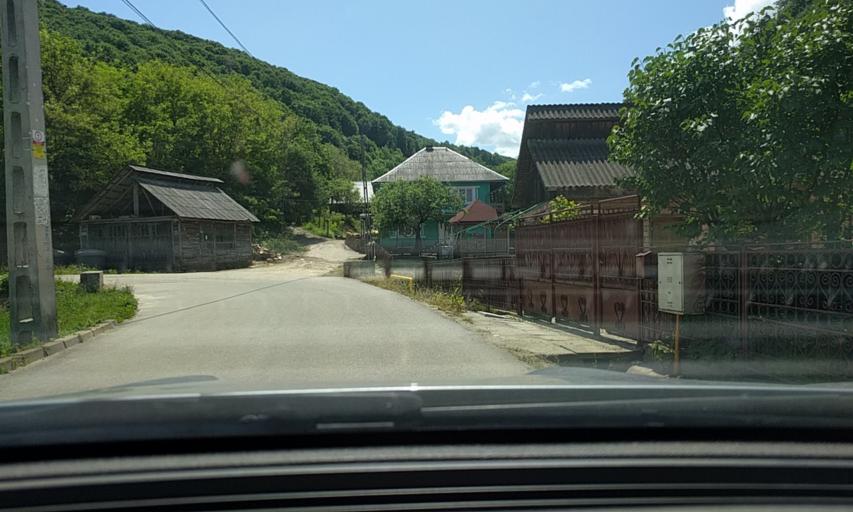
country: RO
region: Bistrita-Nasaud
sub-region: Oras Nasaud
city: Nasaud
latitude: 47.2766
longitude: 24.4117
